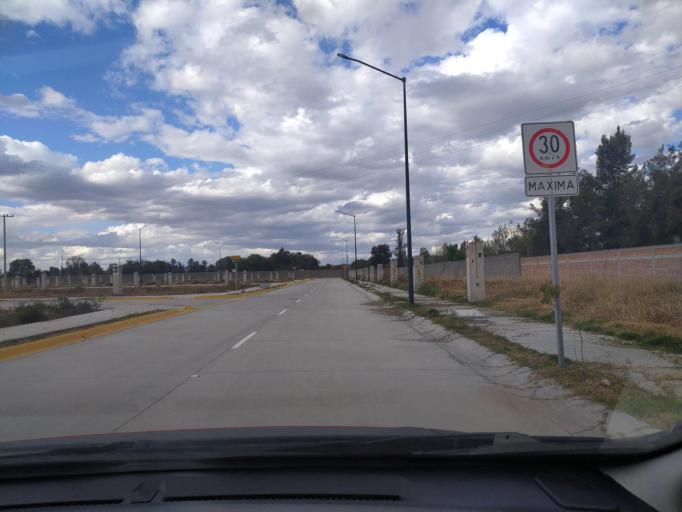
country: LA
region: Oudomxai
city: Muang La
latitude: 21.0243
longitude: 101.8197
